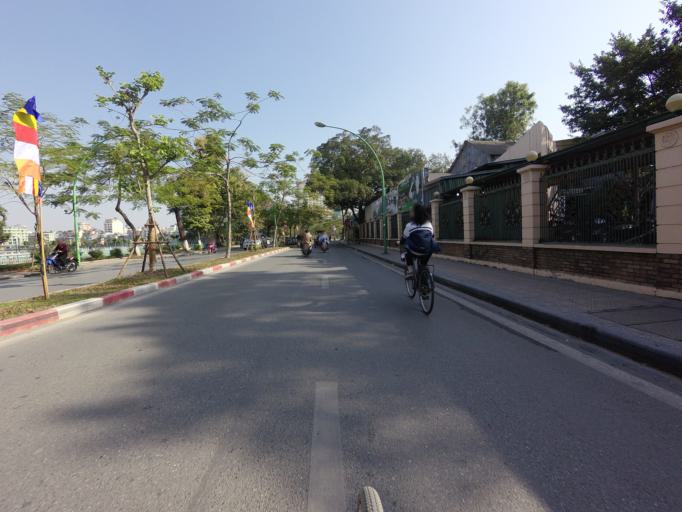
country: VN
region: Ha Noi
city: Hoan Kiem
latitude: 21.0475
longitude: 105.8374
